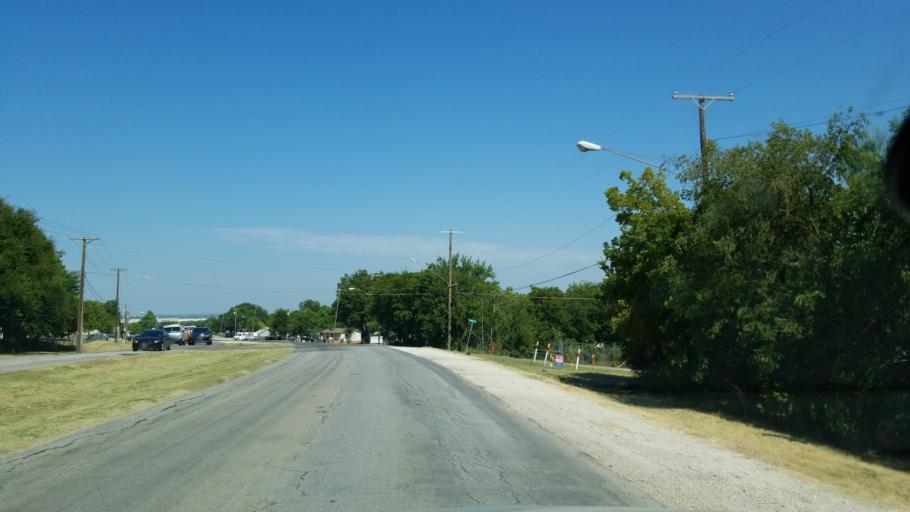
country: US
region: Texas
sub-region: Dallas County
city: Cockrell Hill
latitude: 32.7430
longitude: -96.9037
